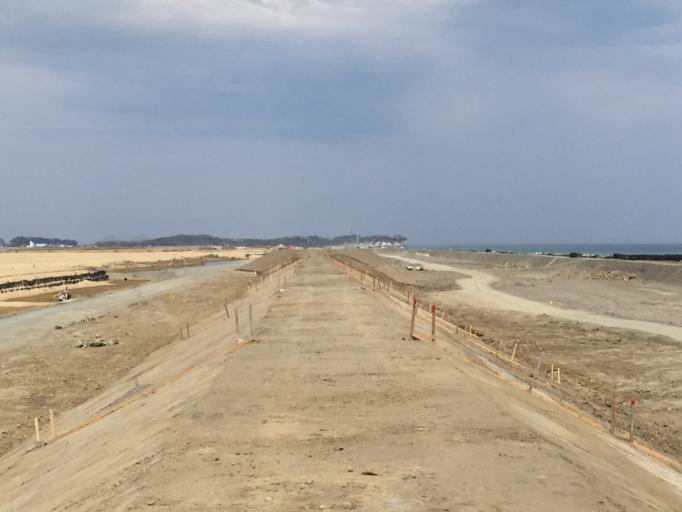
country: JP
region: Miyagi
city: Marumori
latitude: 37.7816
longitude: 140.9870
